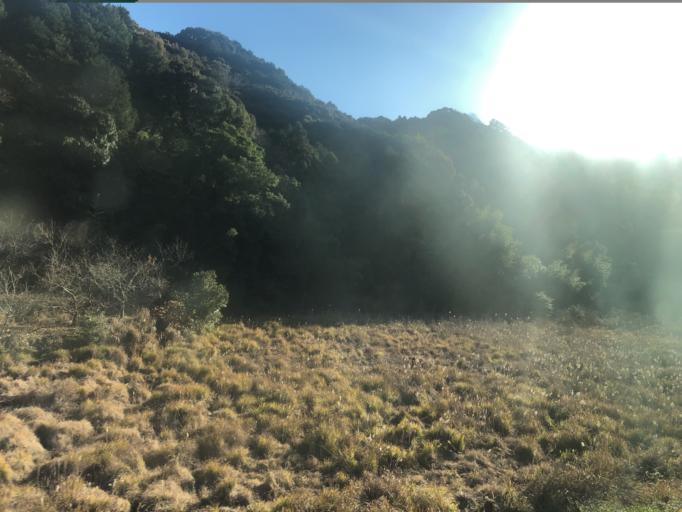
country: JP
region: Kochi
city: Nakamura
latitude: 33.0078
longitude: 132.9847
